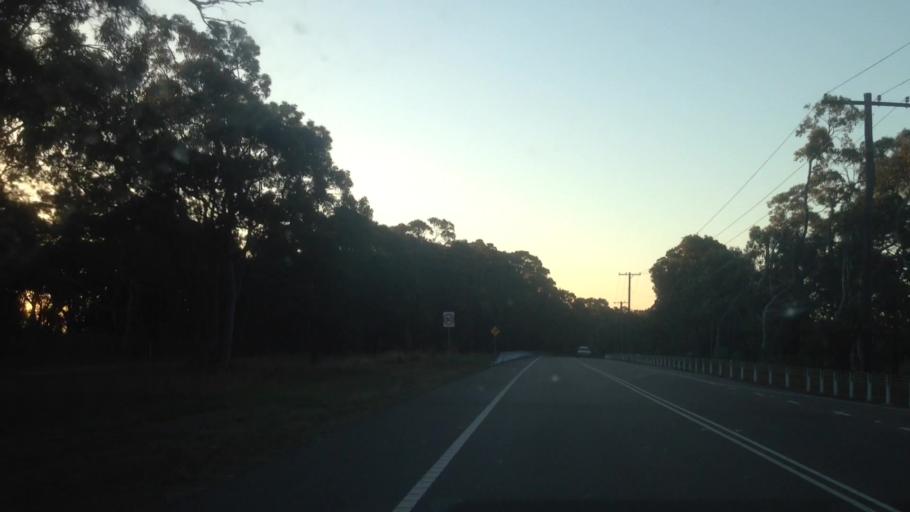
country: AU
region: New South Wales
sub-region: Wyong Shire
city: Kingfisher Shores
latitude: -33.1704
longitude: 151.5356
